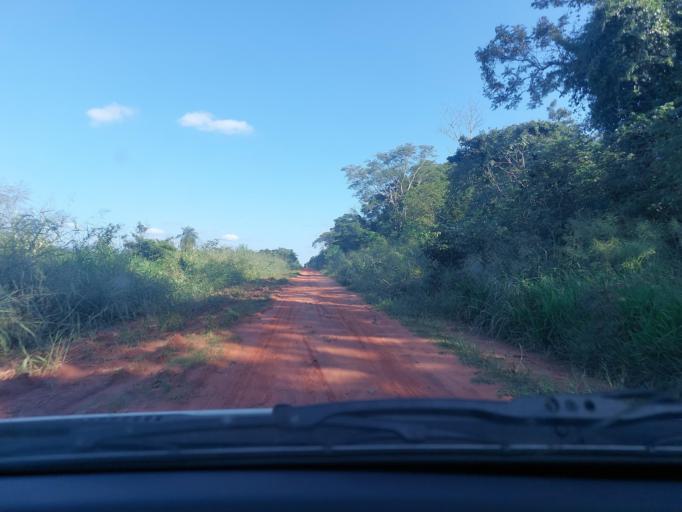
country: PY
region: San Pedro
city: Guayaybi
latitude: -24.5069
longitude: -56.5460
